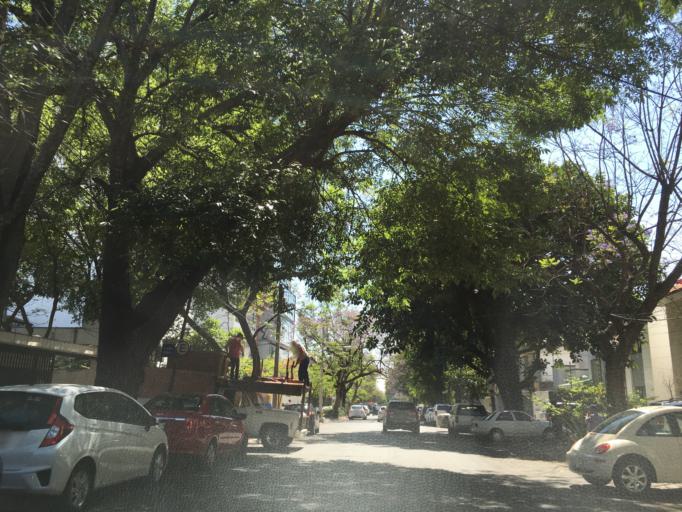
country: MX
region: Jalisco
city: Guadalajara
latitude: 20.6713
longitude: -103.3760
